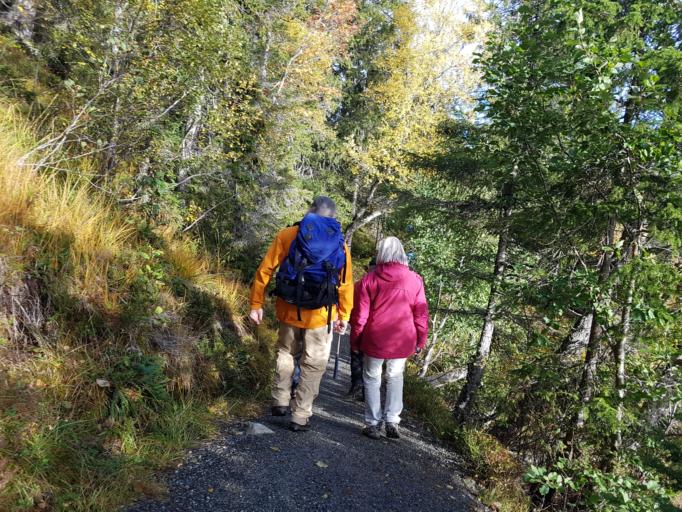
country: NO
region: Sor-Trondelag
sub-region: Trondheim
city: Trondheim
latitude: 63.4248
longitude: 10.2786
